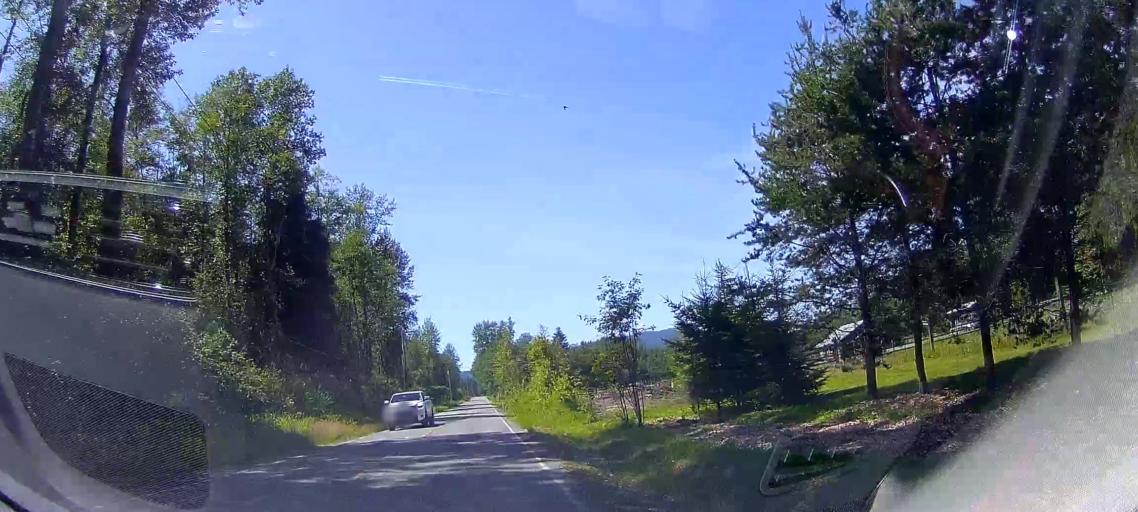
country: US
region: Washington
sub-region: Skagit County
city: Sedro-Woolley
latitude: 48.5900
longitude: -122.3045
